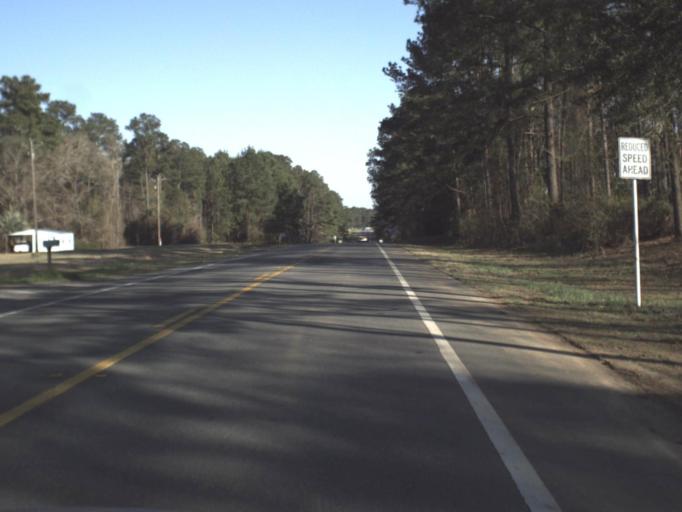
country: US
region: Florida
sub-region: Jackson County
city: Sneads
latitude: 30.7137
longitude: -84.9493
